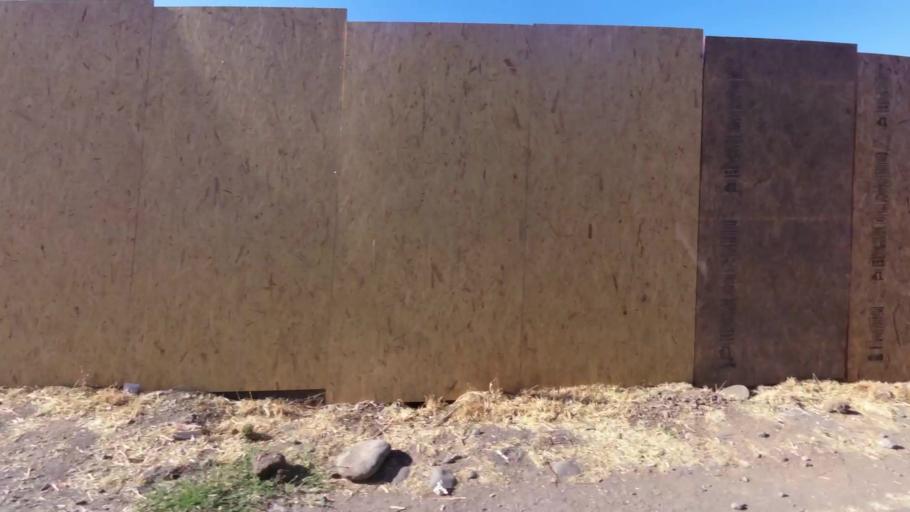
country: CL
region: Maule
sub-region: Provincia de Curico
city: Curico
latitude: -34.9867
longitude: -71.2354
